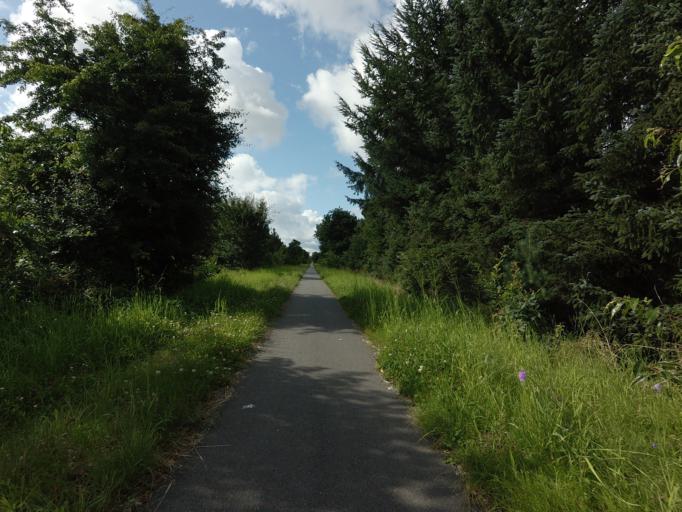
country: DK
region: Central Jutland
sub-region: Silkeborg Kommune
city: Svejbaek
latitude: 56.2075
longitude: 9.6714
